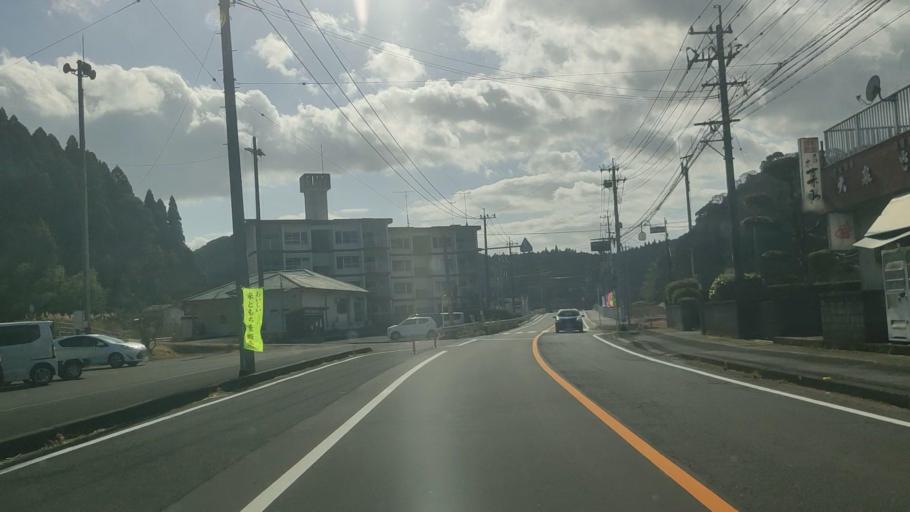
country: JP
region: Kagoshima
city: Okuchi-shinohara
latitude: 31.9430
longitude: 130.7104
